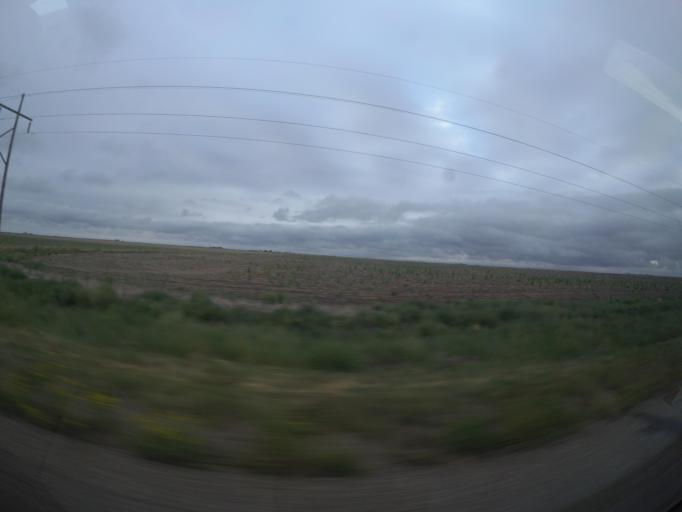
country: US
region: Colorado
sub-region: Yuma County
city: Yuma
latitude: 39.6558
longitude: -102.7269
